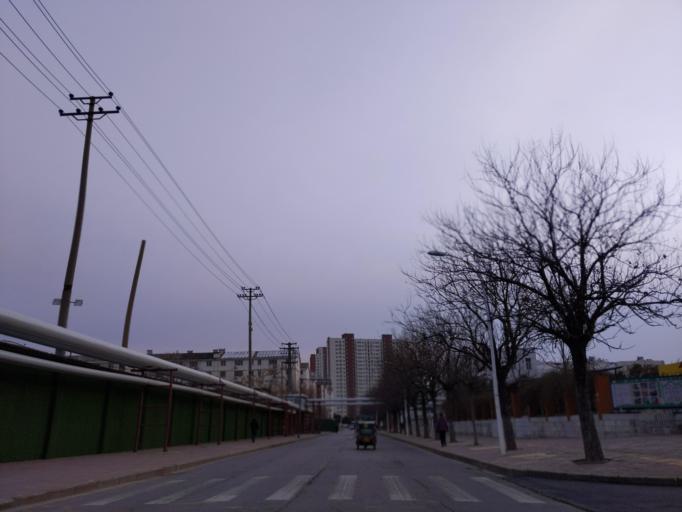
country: CN
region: Henan Sheng
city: Puyang
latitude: 35.7540
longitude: 115.0389
